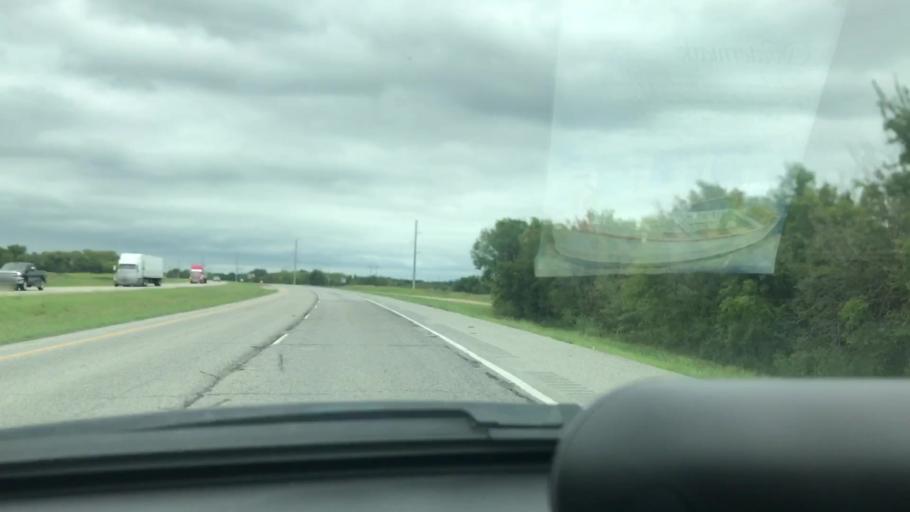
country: US
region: Oklahoma
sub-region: Wagoner County
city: Wagoner
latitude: 35.9957
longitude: -95.3694
